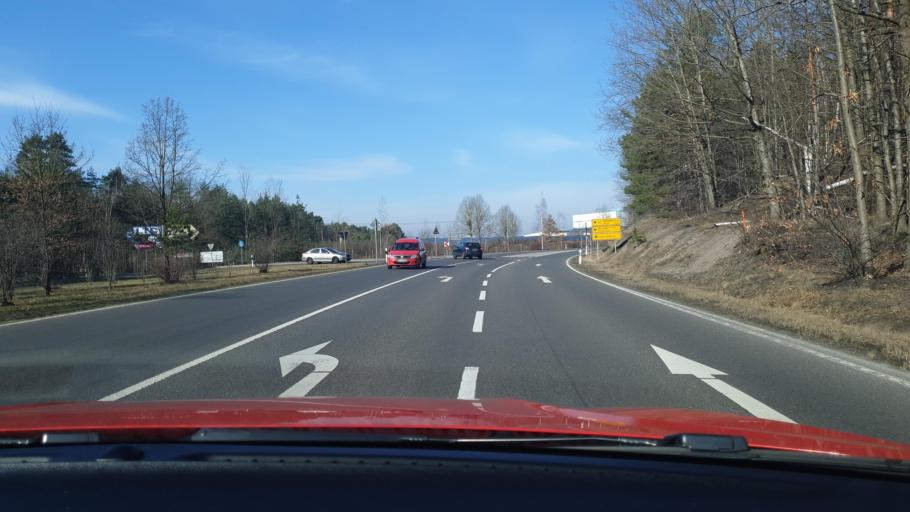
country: DE
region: Saxony
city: Bernsdorf
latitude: 51.4454
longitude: 14.1201
